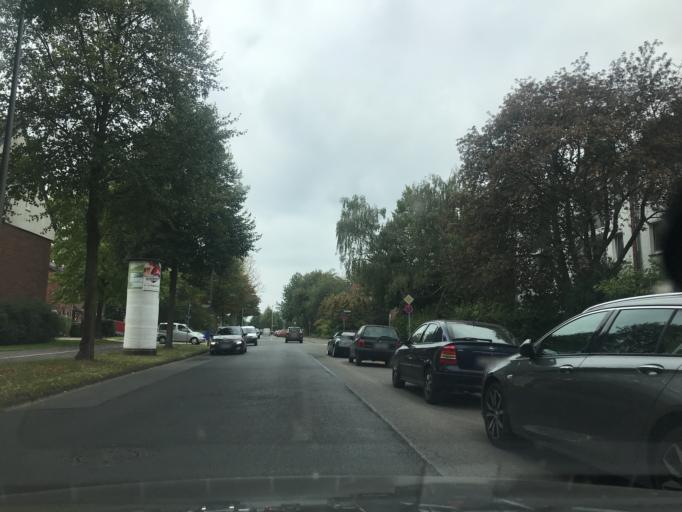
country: DE
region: North Rhine-Westphalia
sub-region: Regierungsbezirk Dusseldorf
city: Krefeld
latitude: 51.3632
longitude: 6.6129
